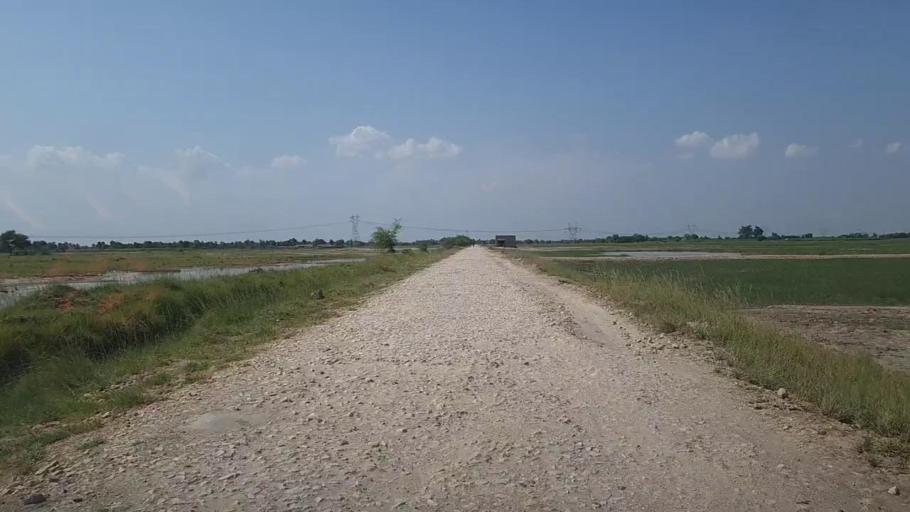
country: PK
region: Sindh
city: Khairpur
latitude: 28.1022
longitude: 69.6249
